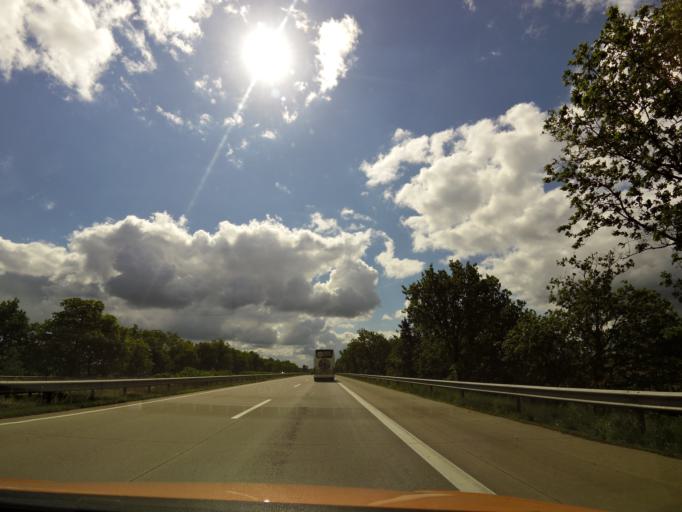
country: DE
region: Lower Saxony
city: Verden
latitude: 52.9563
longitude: 9.2481
